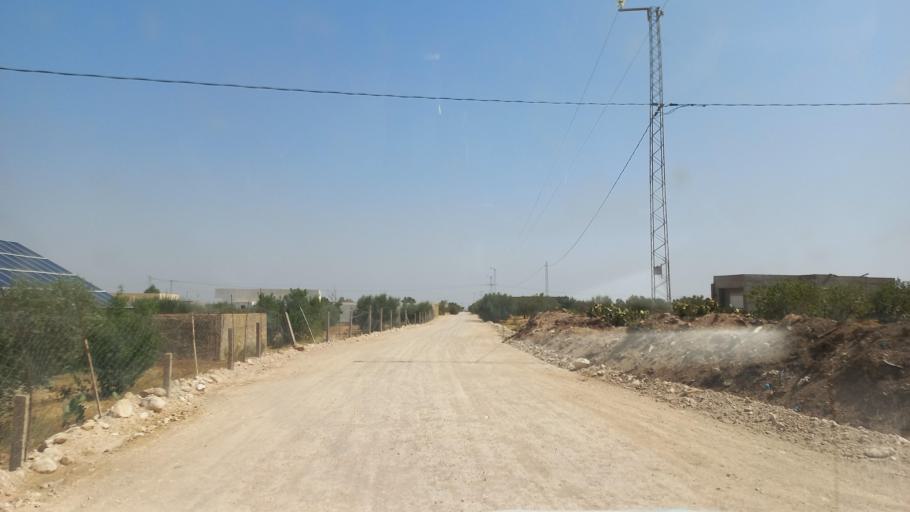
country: TN
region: Al Qasrayn
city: Kasserine
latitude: 35.2599
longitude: 9.0110
